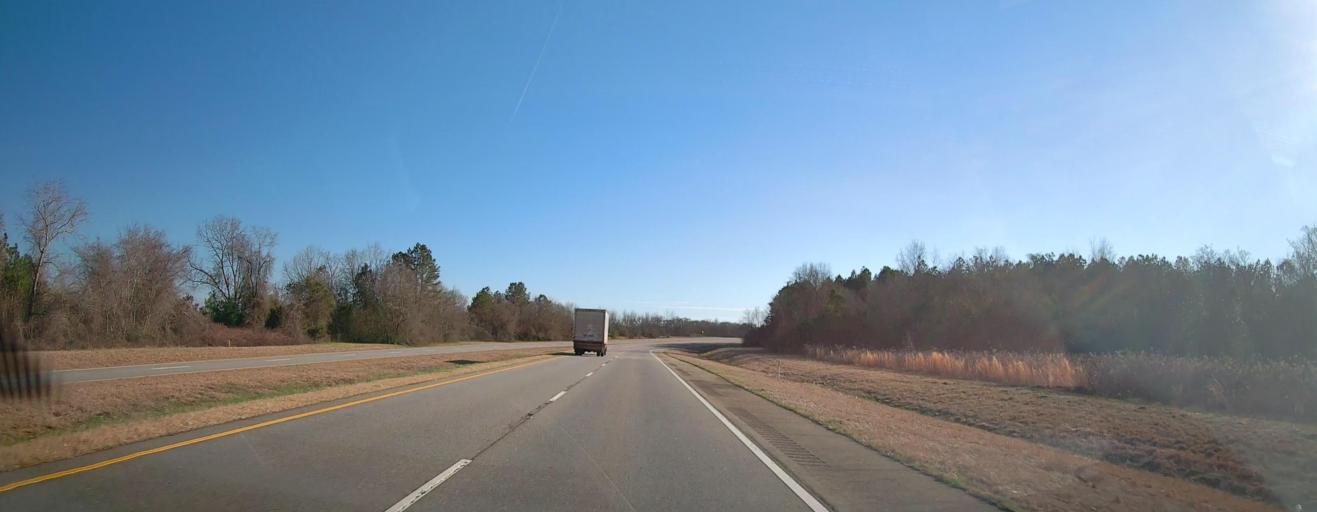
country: US
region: Georgia
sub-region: Sumter County
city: Americus
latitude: 31.9414
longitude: -84.2557
